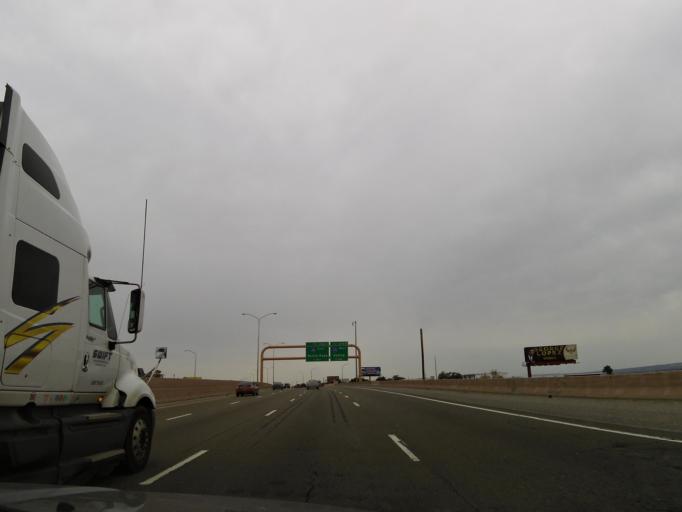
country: US
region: New Mexico
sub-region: Bernalillo County
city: Lee Acres
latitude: 35.1239
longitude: -106.6221
